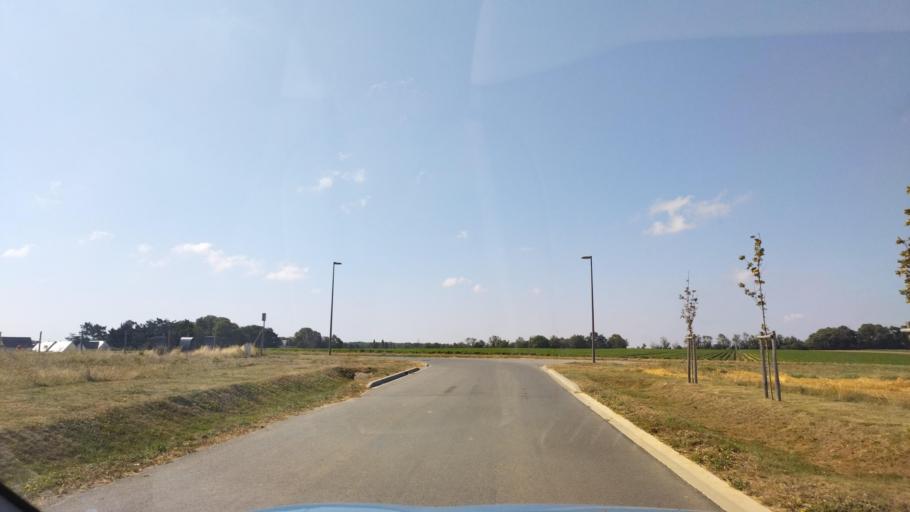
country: FR
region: Lower Normandy
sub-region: Departement du Calvados
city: Douvres-la-Delivrande
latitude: 49.2976
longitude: -0.3934
